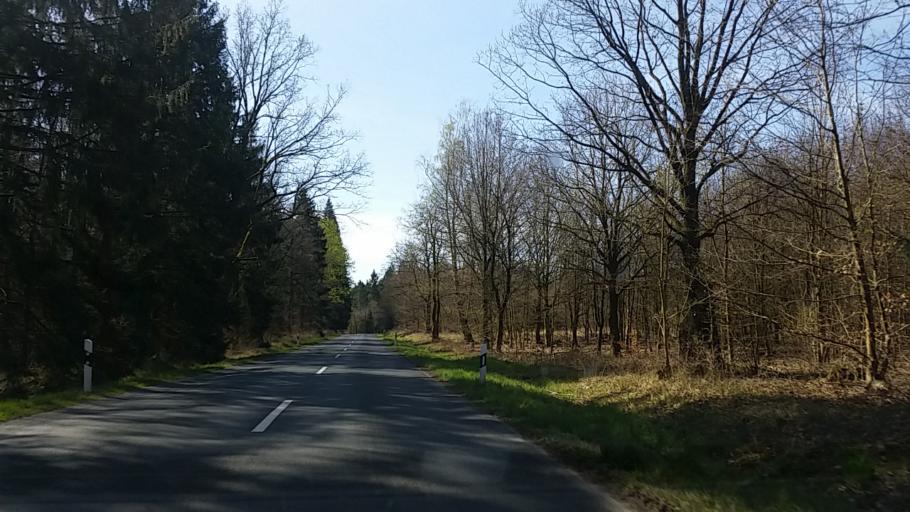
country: DE
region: Lower Saxony
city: Rabke
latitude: 52.1730
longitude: 10.8572
